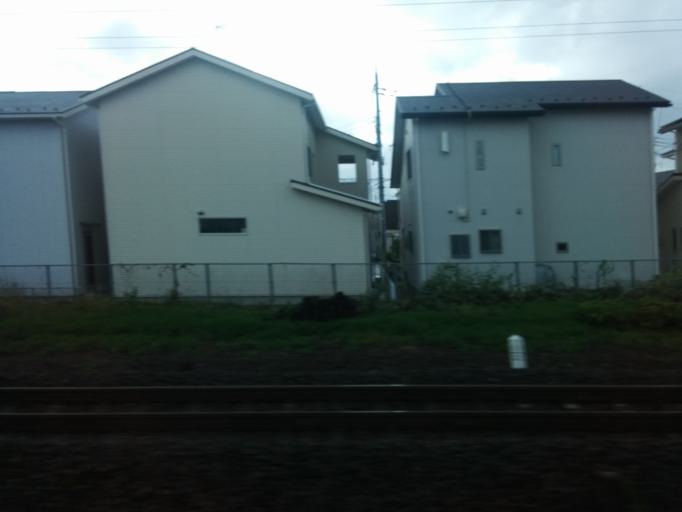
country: JP
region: Shiga Prefecture
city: Moriyama
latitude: 35.0474
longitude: 135.9921
